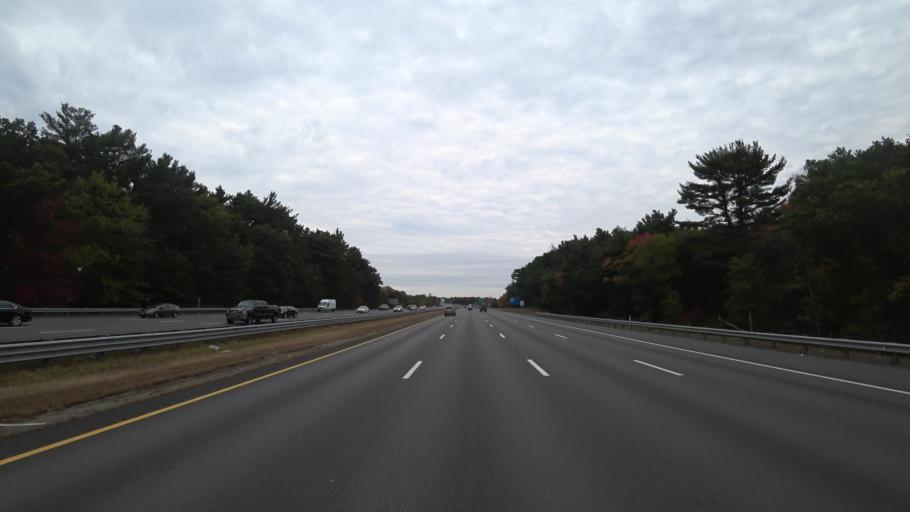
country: US
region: Massachusetts
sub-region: Middlesex County
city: Wilmington
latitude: 42.5468
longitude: -71.1359
